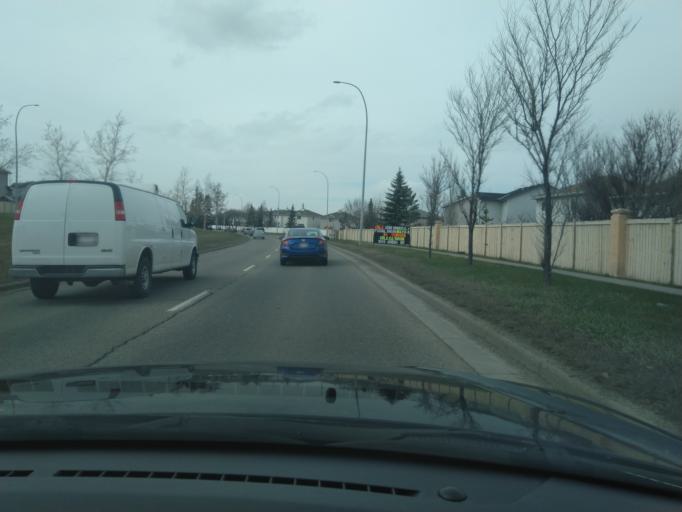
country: CA
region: Alberta
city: Calgary
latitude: 51.1504
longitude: -114.0634
